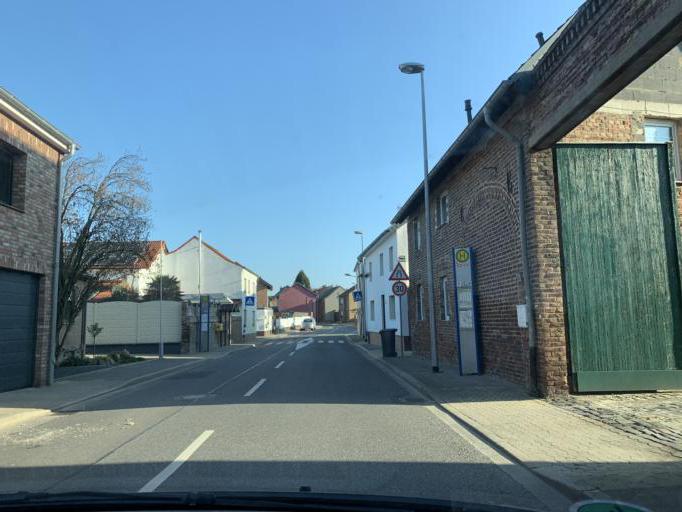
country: DE
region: North Rhine-Westphalia
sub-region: Regierungsbezirk Koln
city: Titz
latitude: 50.9978
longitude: 6.4876
